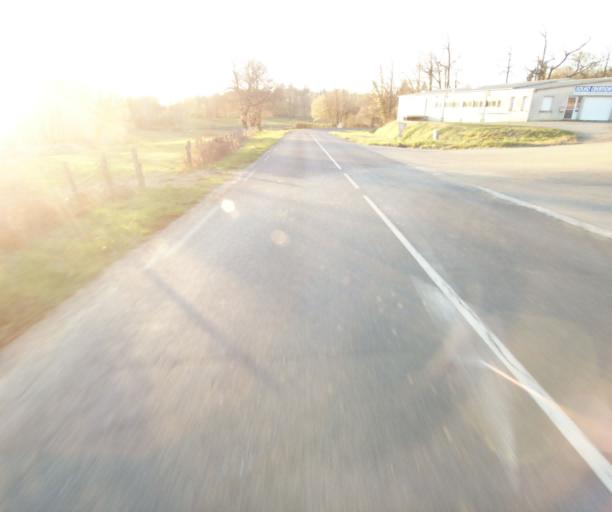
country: FR
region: Limousin
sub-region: Departement de la Correze
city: Saint-Clement
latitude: 45.3318
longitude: 1.6809
